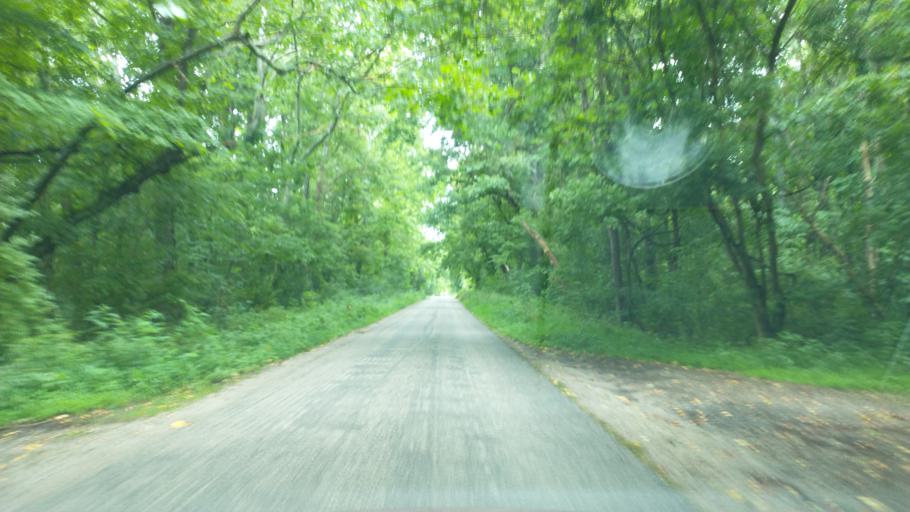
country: US
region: Ohio
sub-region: Meigs County
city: Middleport
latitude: 38.9332
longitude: -82.0779
